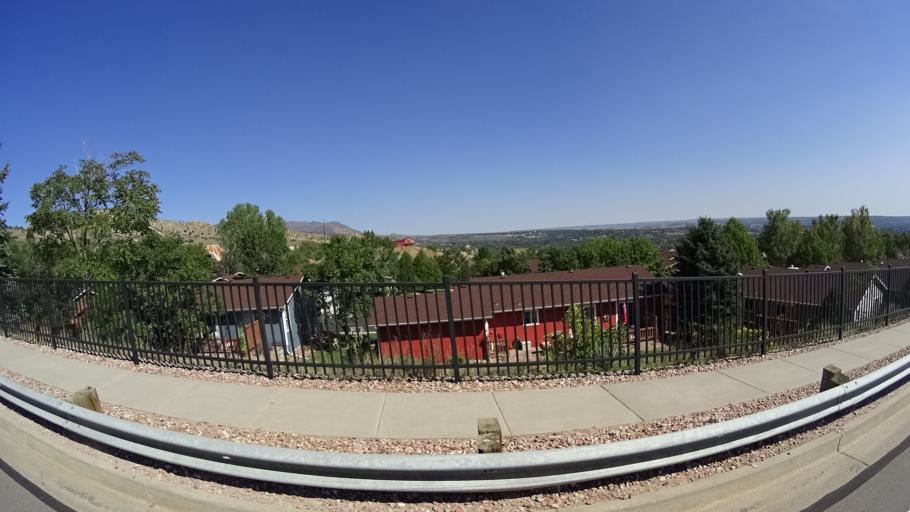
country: US
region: Colorado
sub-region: El Paso County
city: Manitou Springs
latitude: 38.8305
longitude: -104.8760
